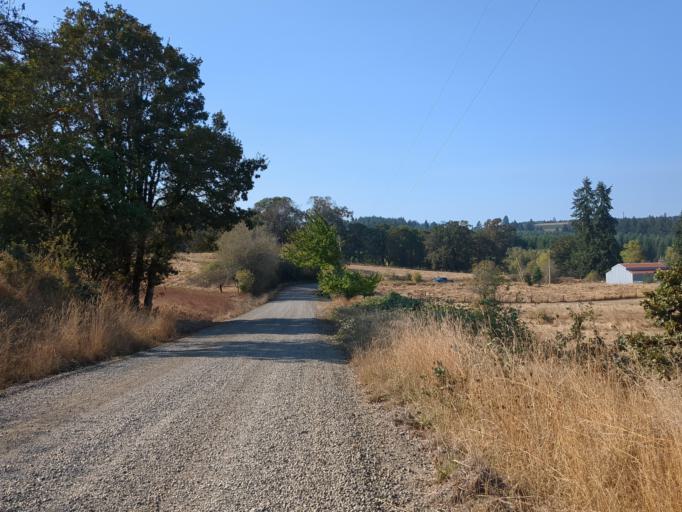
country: US
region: Oregon
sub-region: Lane County
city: Junction City
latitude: 44.2952
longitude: -123.3622
